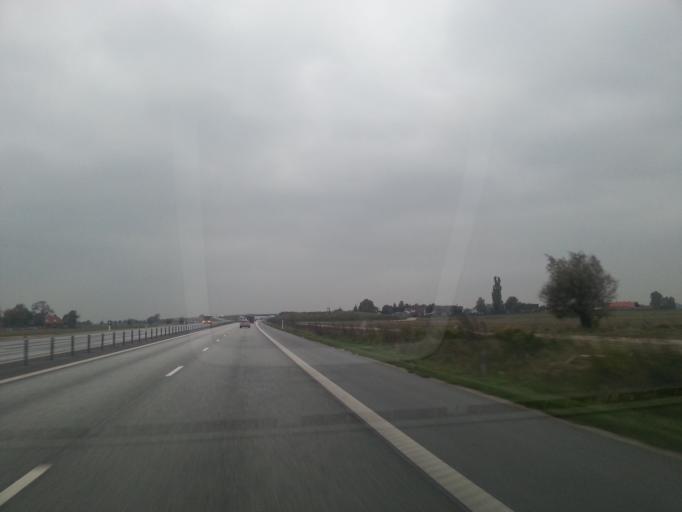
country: SE
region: Skane
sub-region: Vellinge Kommun
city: Vellinge
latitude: 55.4487
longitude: 13.0265
